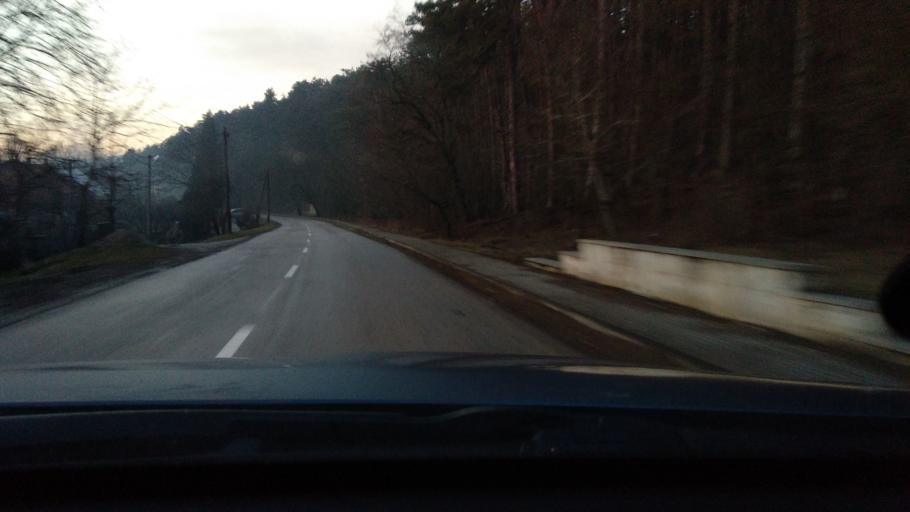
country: SK
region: Nitriansky
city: Trencianske Teplice
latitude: 48.8409
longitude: 18.2586
